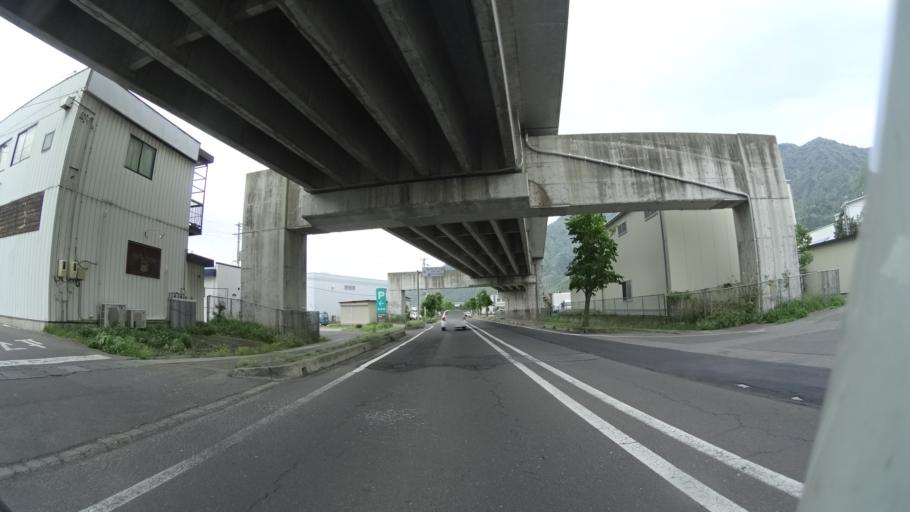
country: JP
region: Nagano
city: Ueda
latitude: 36.4110
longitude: 138.2271
